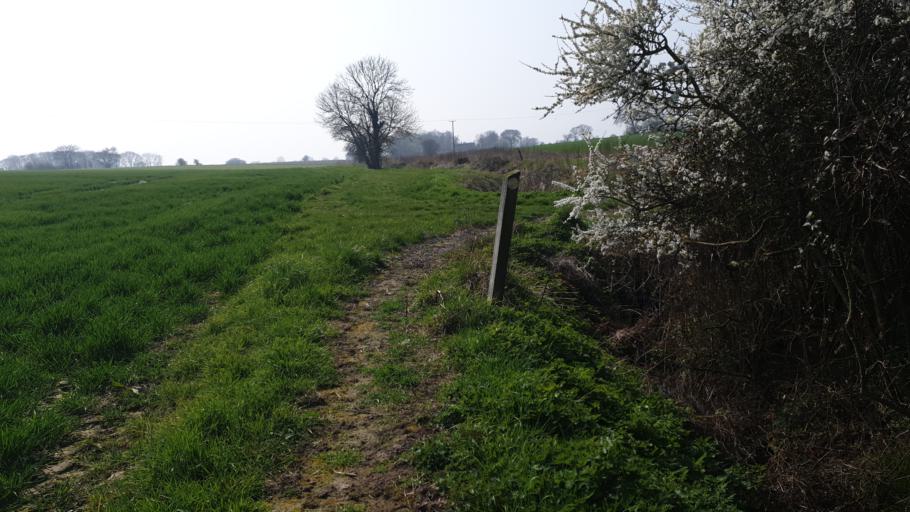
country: GB
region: England
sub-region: Essex
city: Mistley
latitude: 51.9324
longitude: 1.1687
